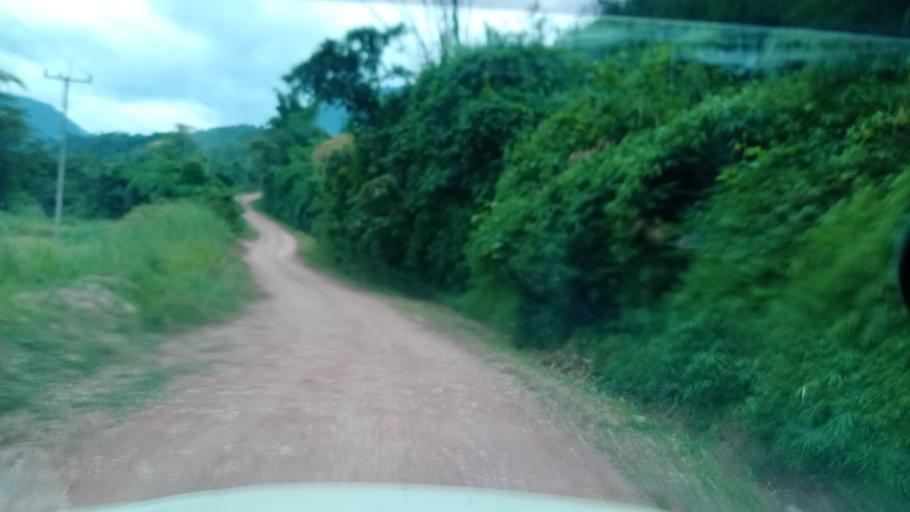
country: TH
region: Changwat Bueng Kan
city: Pak Khat
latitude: 18.7205
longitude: 103.2281
